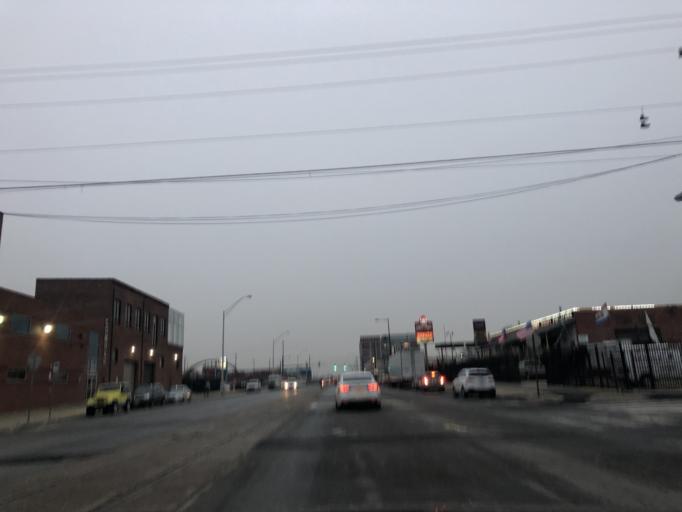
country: US
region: Pennsylvania
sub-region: Philadelphia County
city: Philadelphia
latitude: 39.9898
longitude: -75.1366
